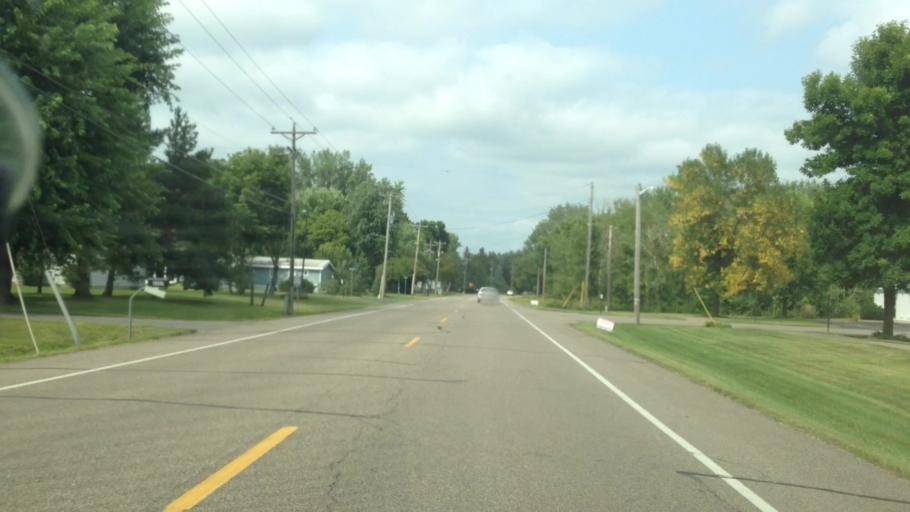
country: US
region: Minnesota
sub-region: Anoka County
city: Circle Pines
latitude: 45.1340
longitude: -93.1273
